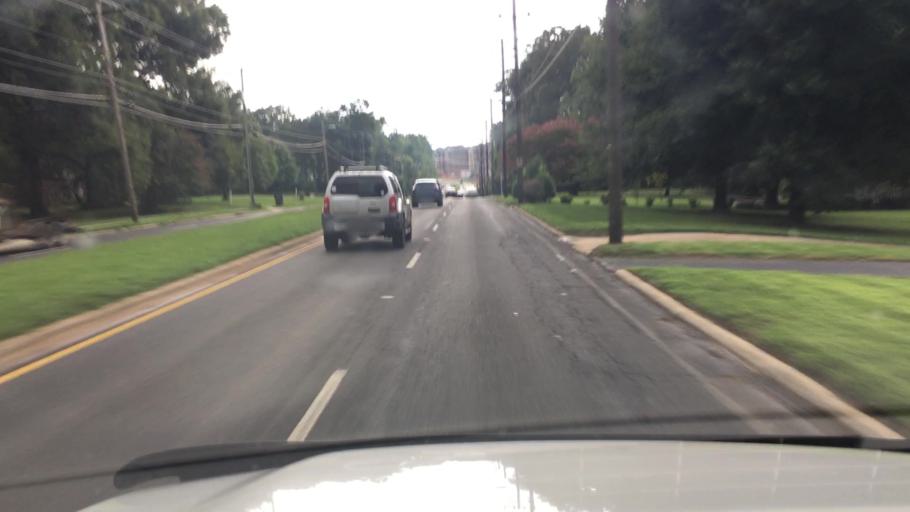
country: US
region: North Carolina
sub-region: Mecklenburg County
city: Charlotte
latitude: 35.1625
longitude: -80.8013
